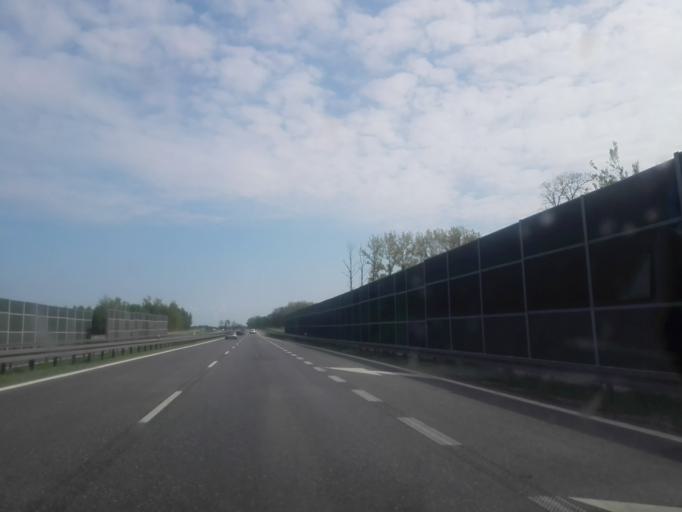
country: PL
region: Masovian Voivodeship
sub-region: Powiat zyrardowski
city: Mszczonow
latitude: 51.9553
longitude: 20.4947
